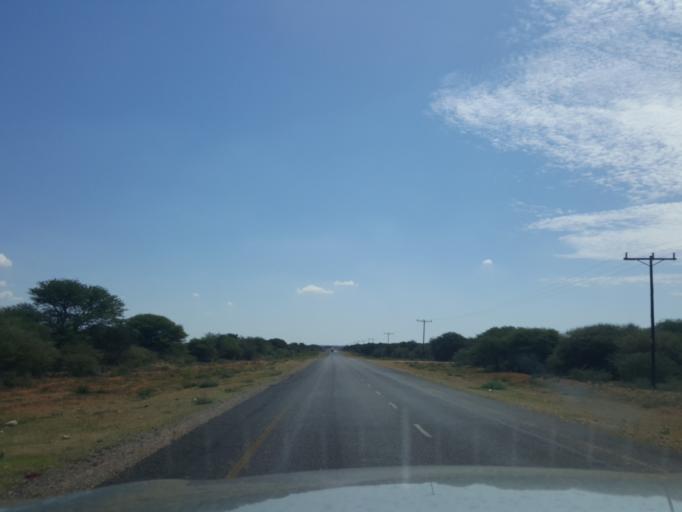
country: BW
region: Kweneng
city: Letlhakeng
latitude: -24.1204
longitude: 25.0736
